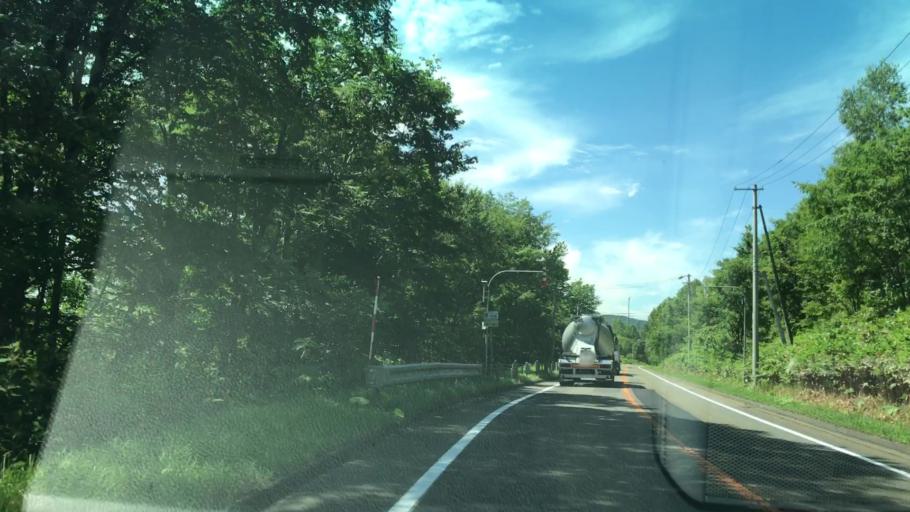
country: JP
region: Hokkaido
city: Shimo-furano
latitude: 42.9117
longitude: 142.4466
